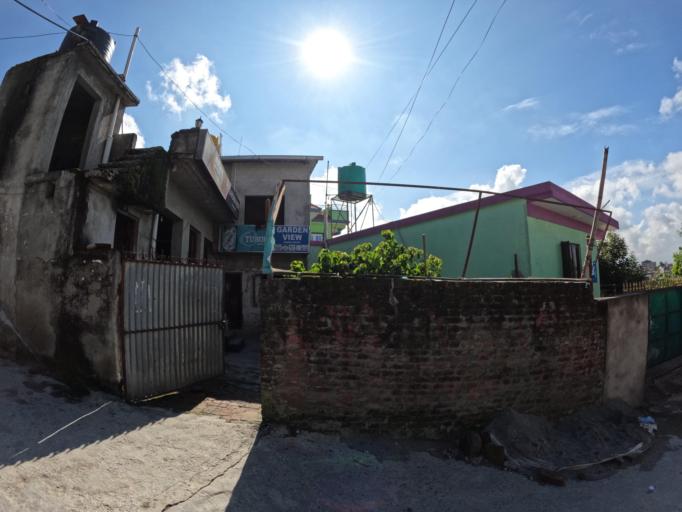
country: NP
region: Central Region
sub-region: Bagmati Zone
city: Kathmandu
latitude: 27.7478
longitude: 85.3357
